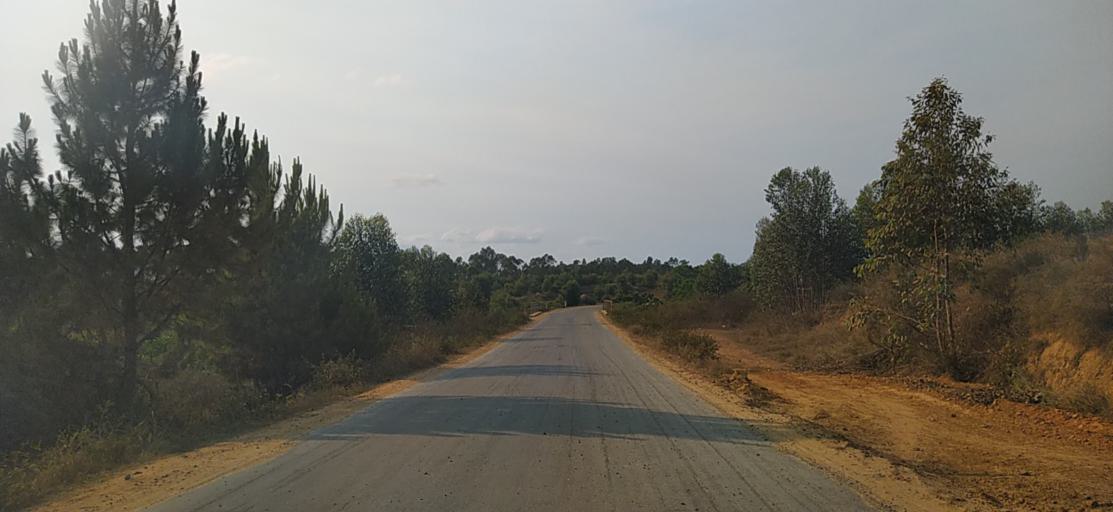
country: MG
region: Alaotra Mangoro
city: Moramanga
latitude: -18.6536
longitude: 48.2742
